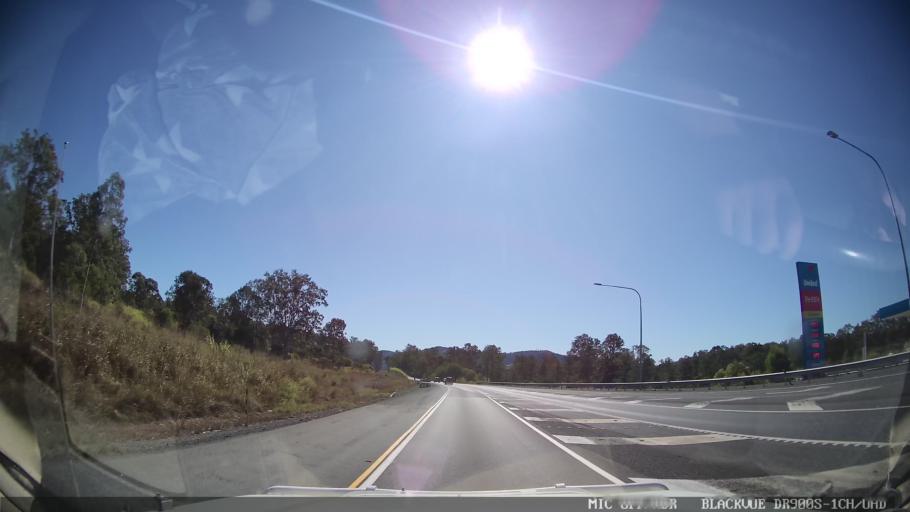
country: AU
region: Queensland
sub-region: Gympie Regional Council
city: Gympie
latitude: -26.0057
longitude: 152.5663
